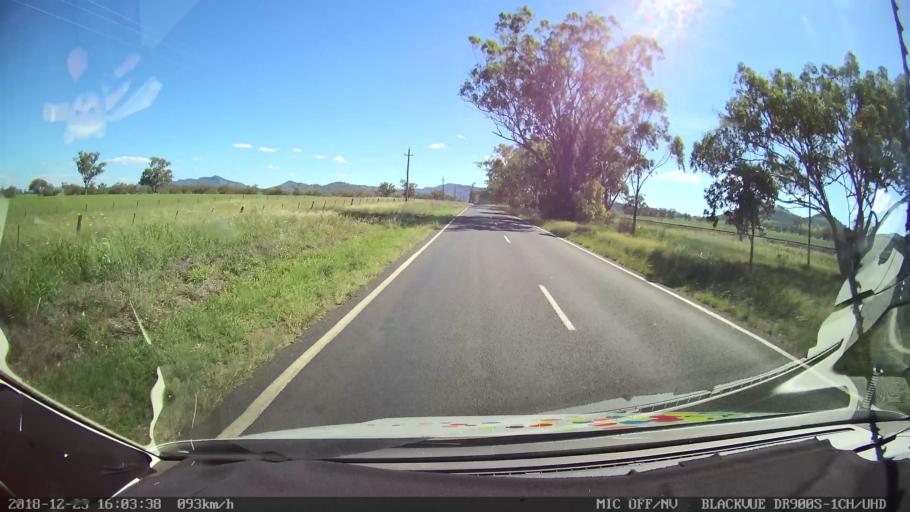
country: AU
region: New South Wales
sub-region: Tamworth Municipality
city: Phillip
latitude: -31.2454
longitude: 150.7990
